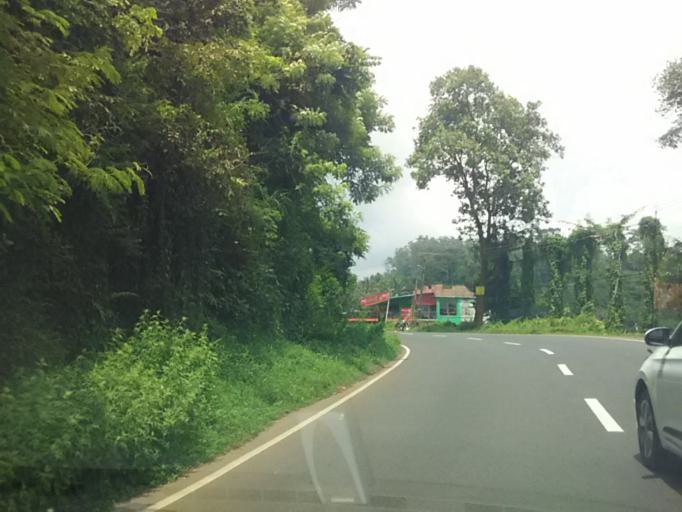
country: IN
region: Kerala
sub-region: Wayanad
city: Kalpetta
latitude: 11.5596
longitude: 76.0400
